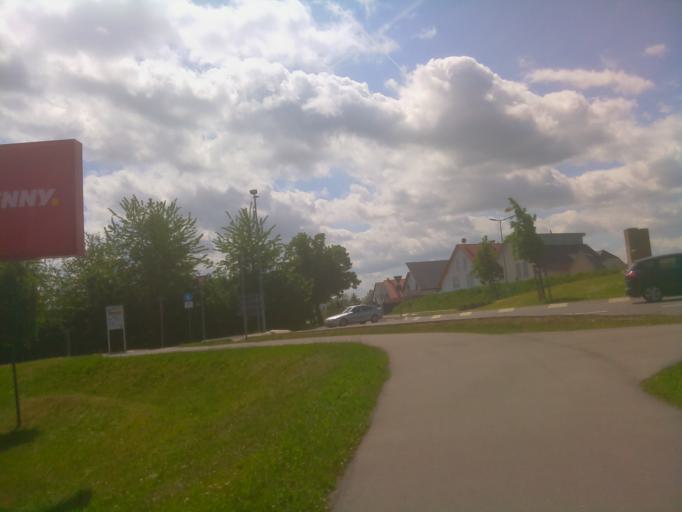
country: DE
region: Rheinland-Pfalz
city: Waldsee
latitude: 49.4056
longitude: 8.4352
